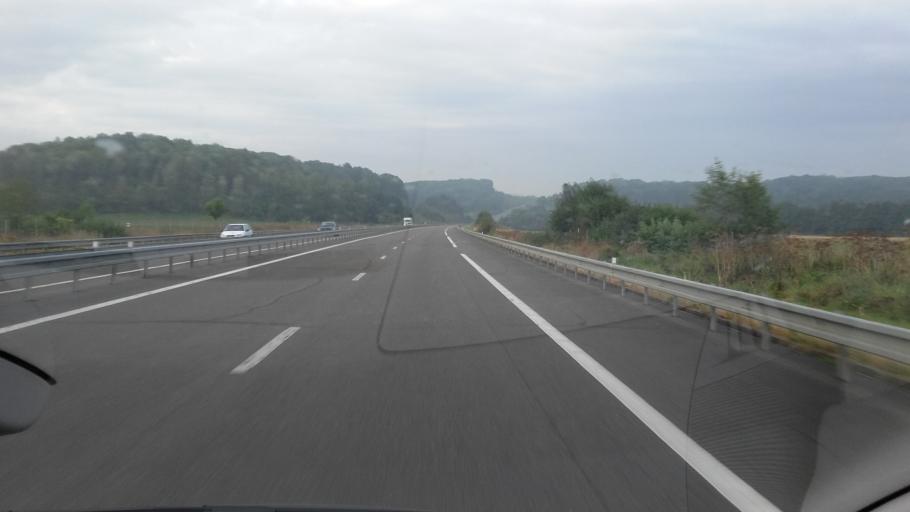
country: FR
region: Champagne-Ardenne
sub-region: Departement des Ardennes
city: Attigny
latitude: 49.6222
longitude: 4.5494
